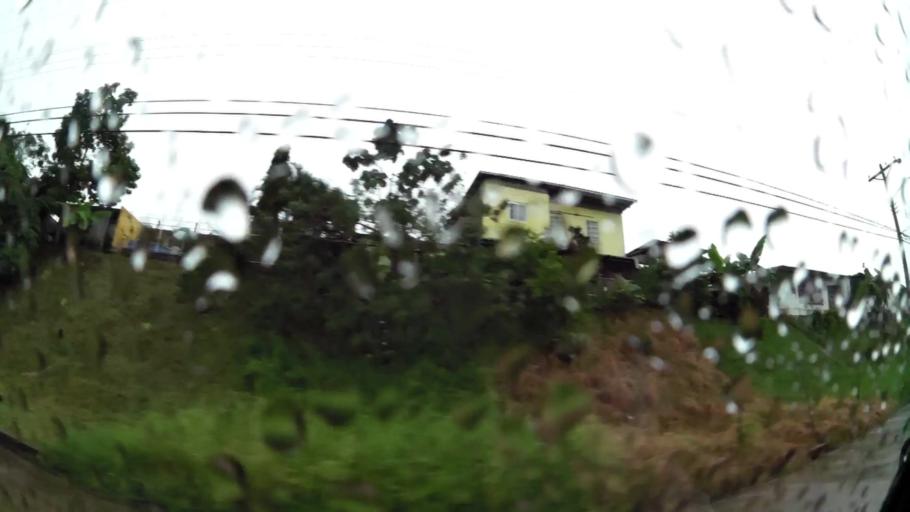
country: PA
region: Panama
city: San Miguelito
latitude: 9.0523
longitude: -79.4722
